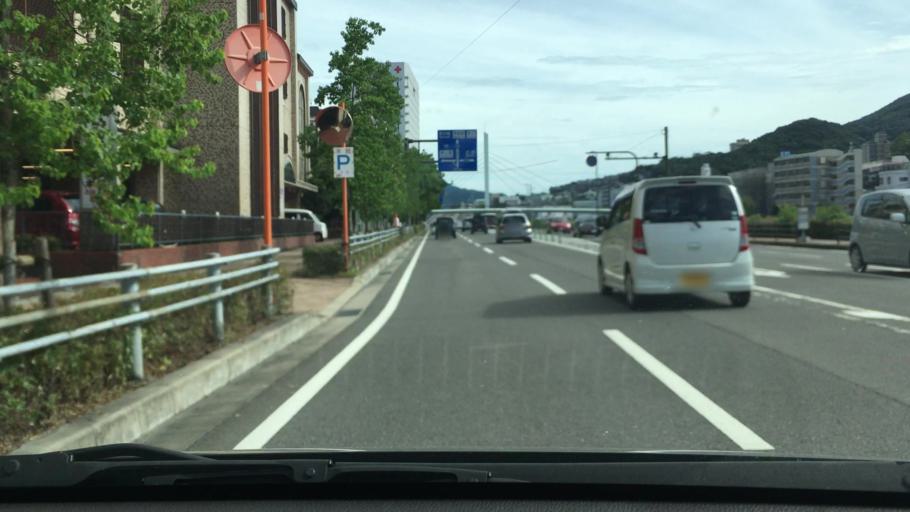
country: JP
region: Nagasaki
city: Nagasaki-shi
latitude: 32.7685
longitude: 129.8624
